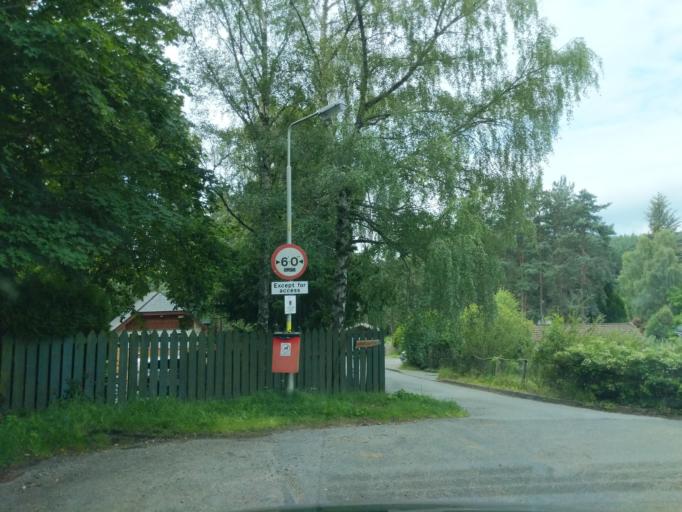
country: GB
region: Scotland
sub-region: Highland
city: Grantown on Spey
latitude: 57.3253
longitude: -3.6119
